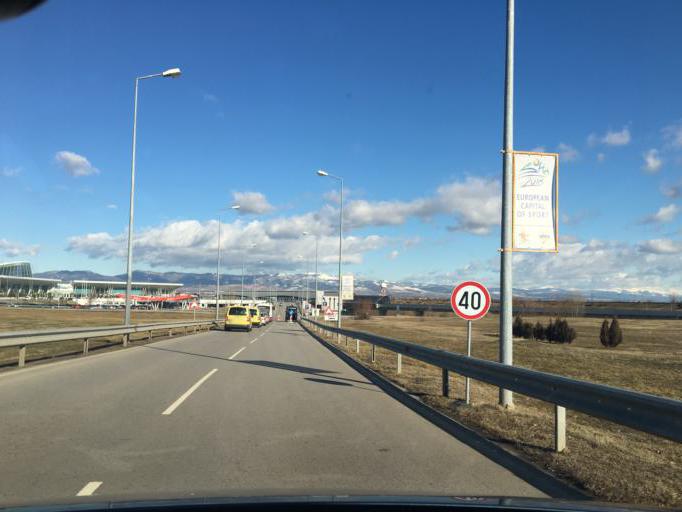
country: BG
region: Sofia-Capital
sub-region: Stolichna Obshtina
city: Sofia
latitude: 42.6852
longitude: 23.4122
